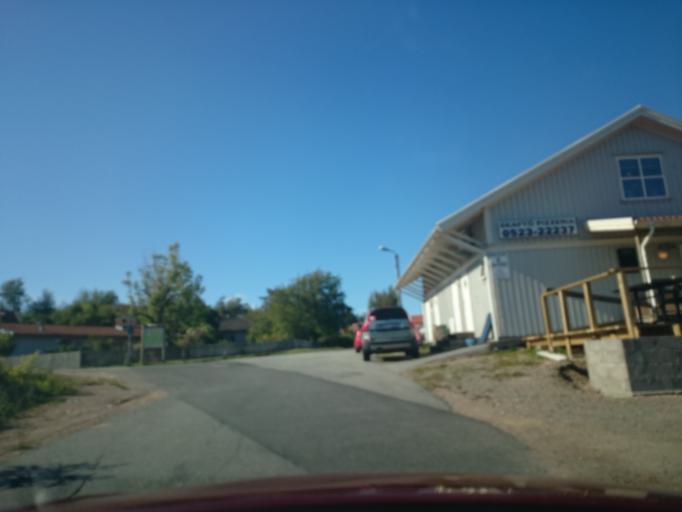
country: SE
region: Vaestra Goetaland
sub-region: Lysekils Kommun
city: Lysekil
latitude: 58.2392
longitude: 11.4570
